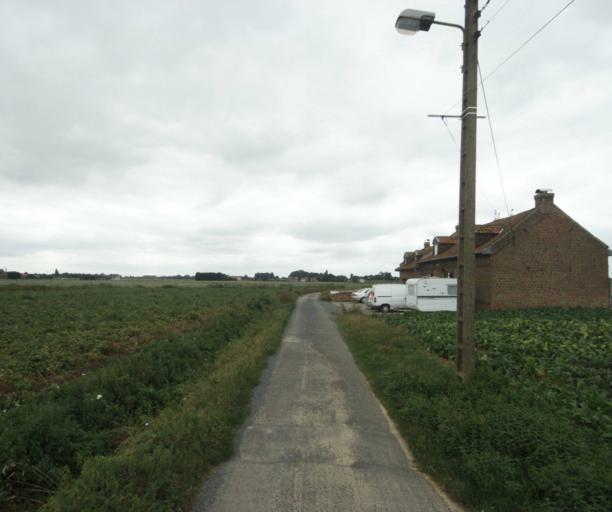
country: FR
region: Nord-Pas-de-Calais
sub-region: Departement du Nord
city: Leers
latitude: 50.6764
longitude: 3.2641
